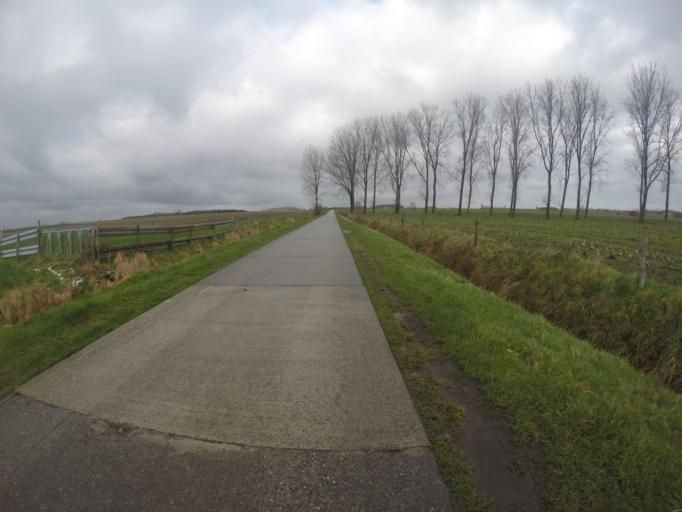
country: BE
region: Flanders
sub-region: Provincie Oost-Vlaanderen
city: Eeklo
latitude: 51.1565
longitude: 3.5058
